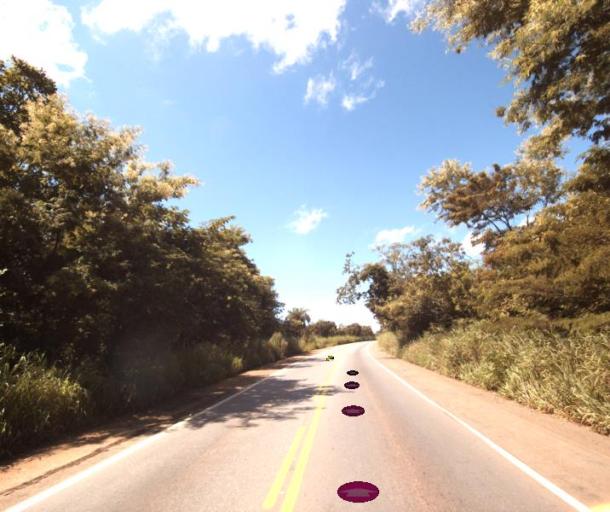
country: BR
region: Goias
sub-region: Jaragua
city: Jaragua
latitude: -15.6804
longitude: -49.3424
